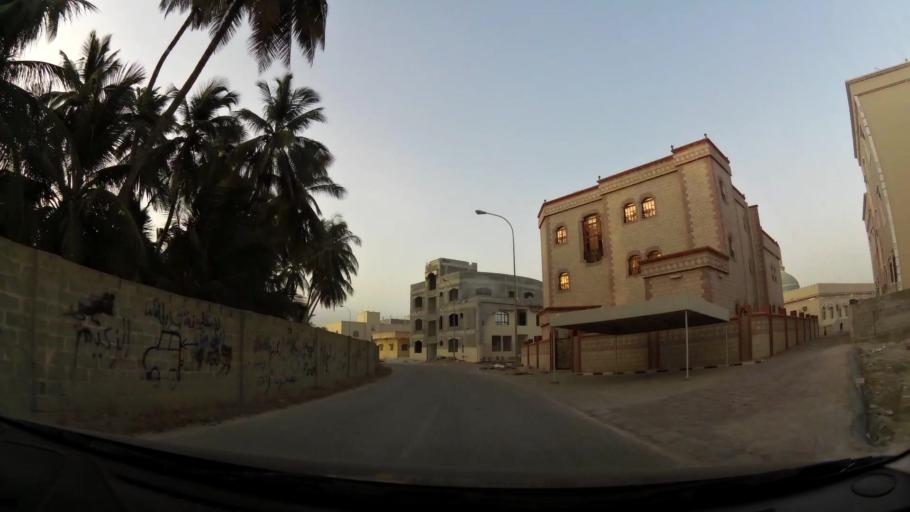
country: OM
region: Zufar
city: Salalah
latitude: 17.0184
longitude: 54.1205
